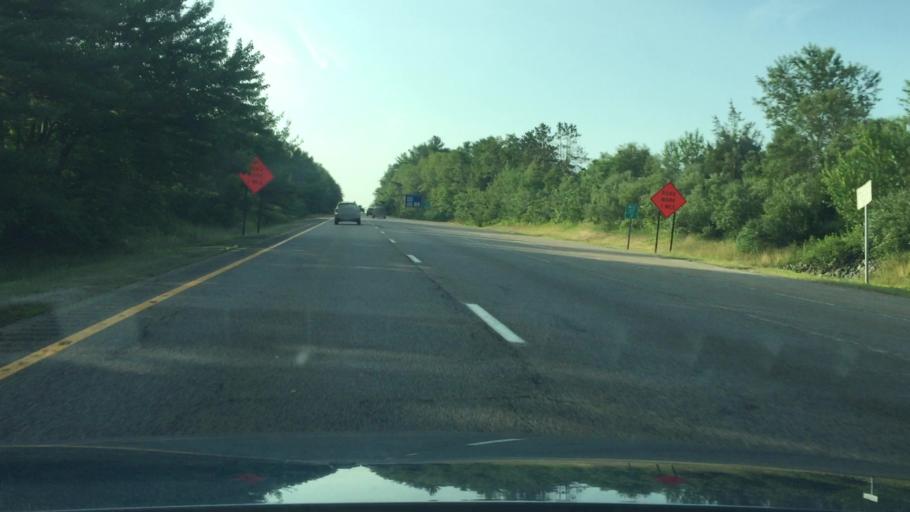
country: US
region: Massachusetts
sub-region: Plymouth County
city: North Pembroke
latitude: 42.1118
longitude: -70.7724
